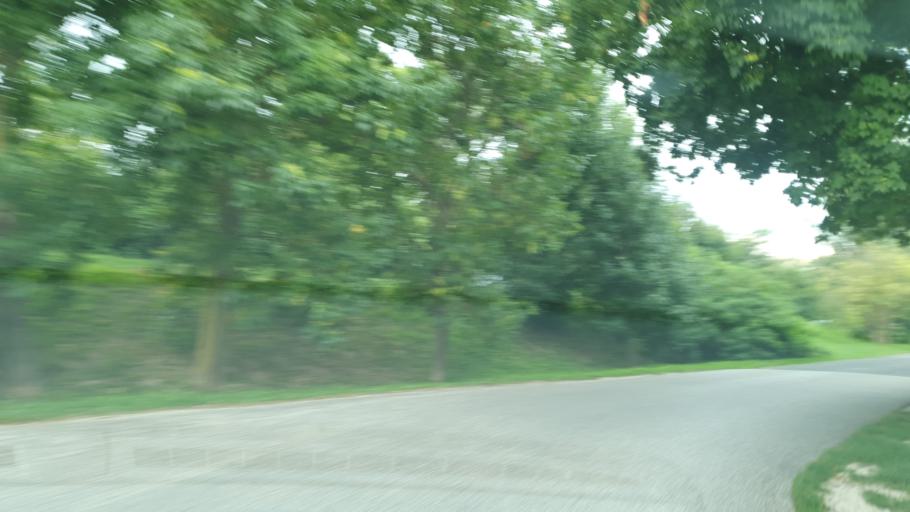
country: HU
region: Somogy
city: Balatonszabadi
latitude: 46.9288
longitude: 18.1213
